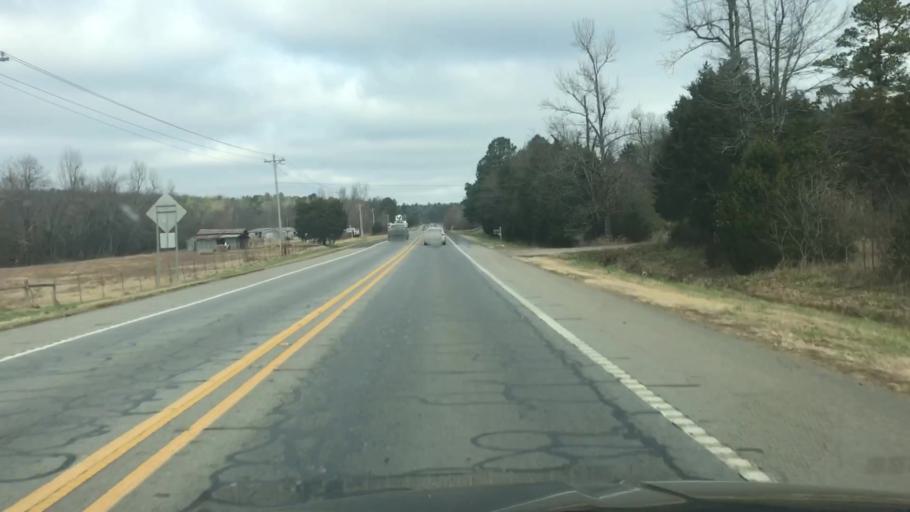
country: US
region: Arkansas
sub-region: Scott County
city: Waldron
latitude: 34.8273
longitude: -94.0391
